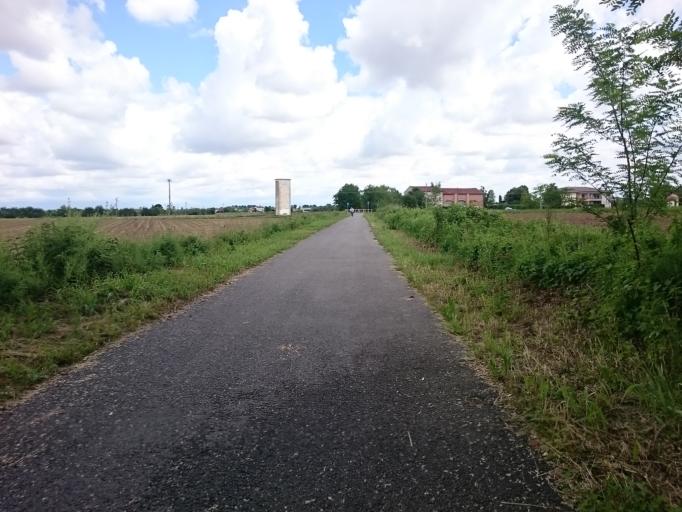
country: IT
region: Veneto
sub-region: Provincia di Padova
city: Campodoro
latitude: 45.5079
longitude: 11.7490
